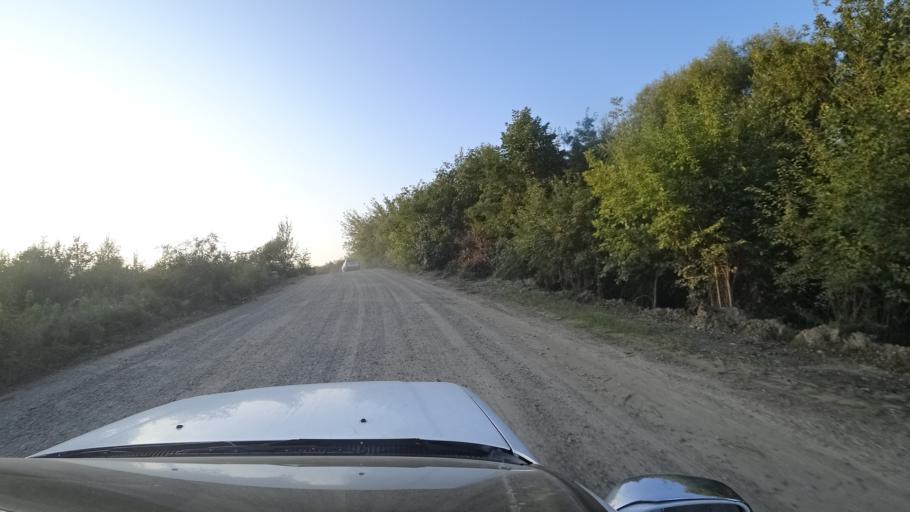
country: RU
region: Primorskiy
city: Dal'nerechensk
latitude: 45.9420
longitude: 133.7611
